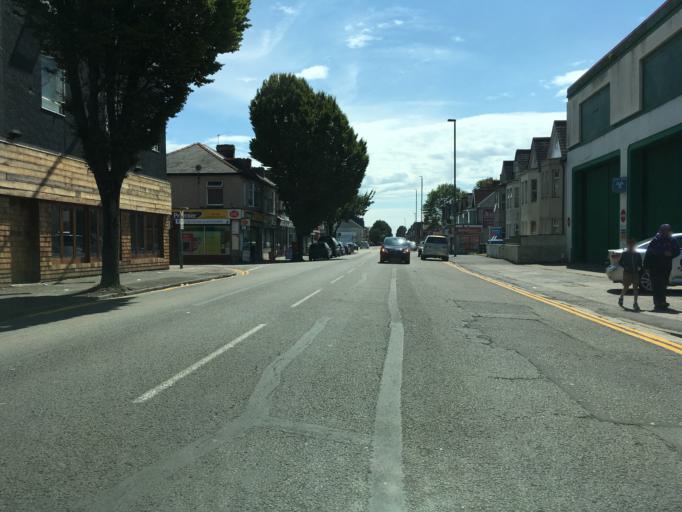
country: GB
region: Wales
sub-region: Newport
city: Newport
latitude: 51.5870
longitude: -2.9832
